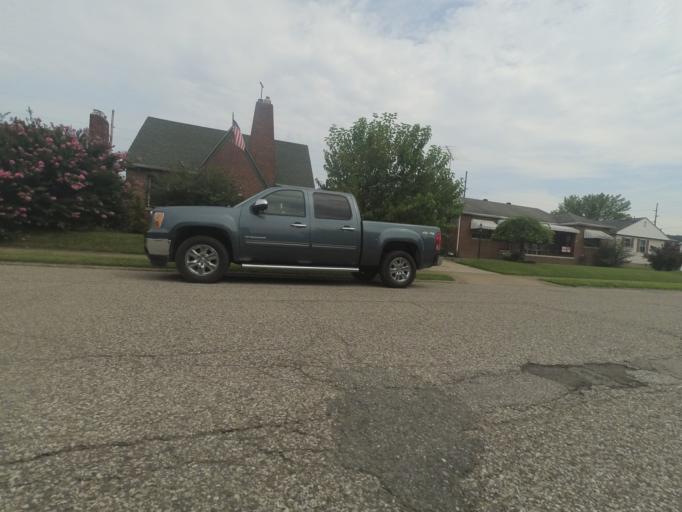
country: US
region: West Virginia
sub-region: Cabell County
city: Huntington
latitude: 38.4264
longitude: -82.4596
